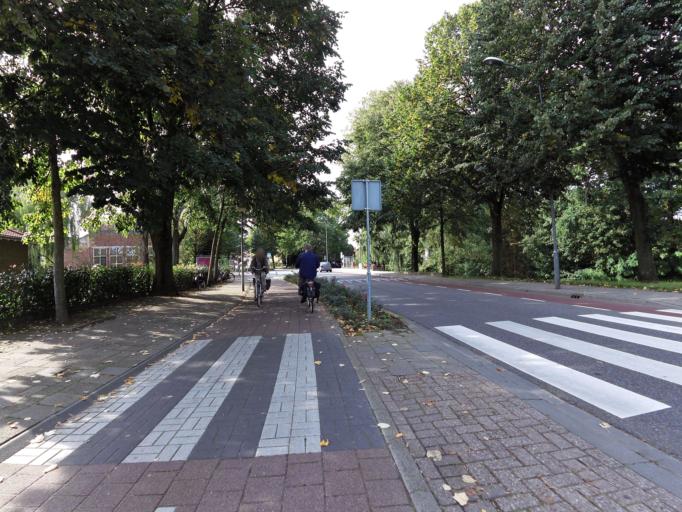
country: NL
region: Gelderland
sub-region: Gemeente Doesburg
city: Doesburg
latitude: 52.0140
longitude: 6.1403
